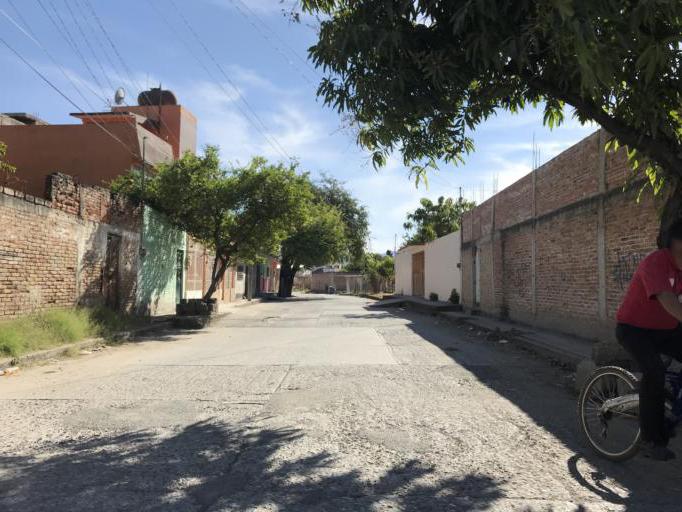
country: MX
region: Guerrero
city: Iguala de la Independencia
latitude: 18.3427
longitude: -99.5468
